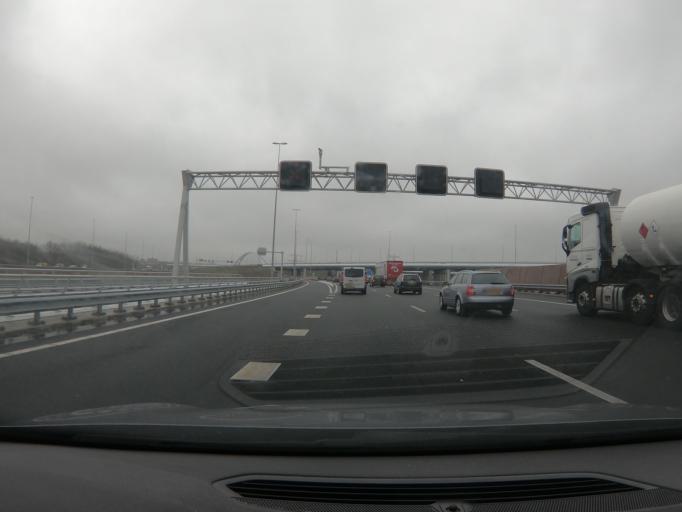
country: NL
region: North Holland
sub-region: Gemeente Naarden
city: Naarden
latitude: 52.3136
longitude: 5.1146
